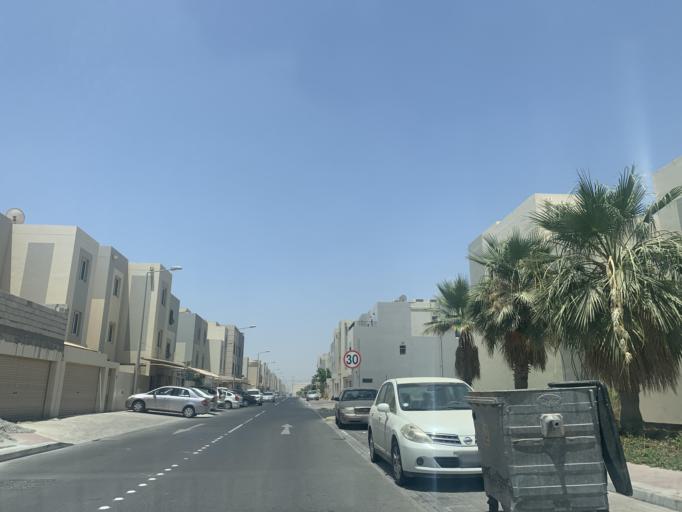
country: BH
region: Manama
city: Jidd Hafs
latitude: 26.2372
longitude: 50.4704
